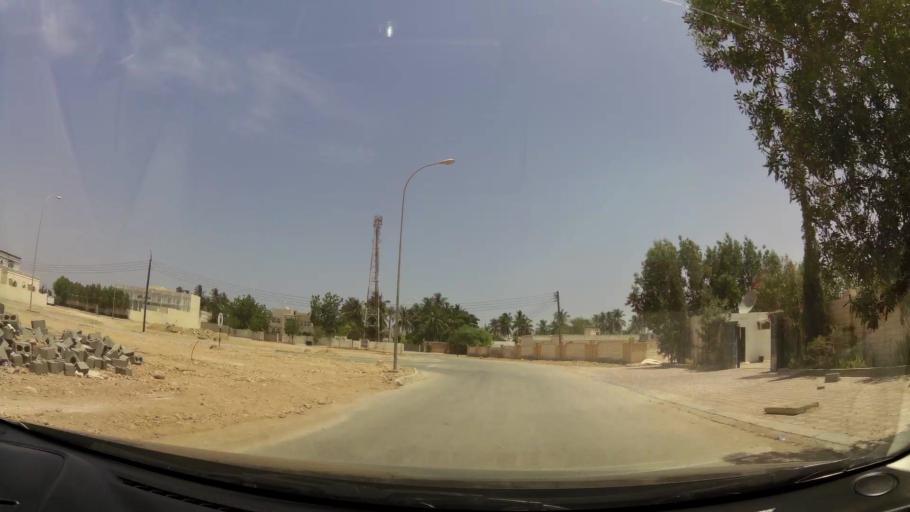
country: OM
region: Zufar
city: Salalah
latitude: 17.0637
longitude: 54.1538
